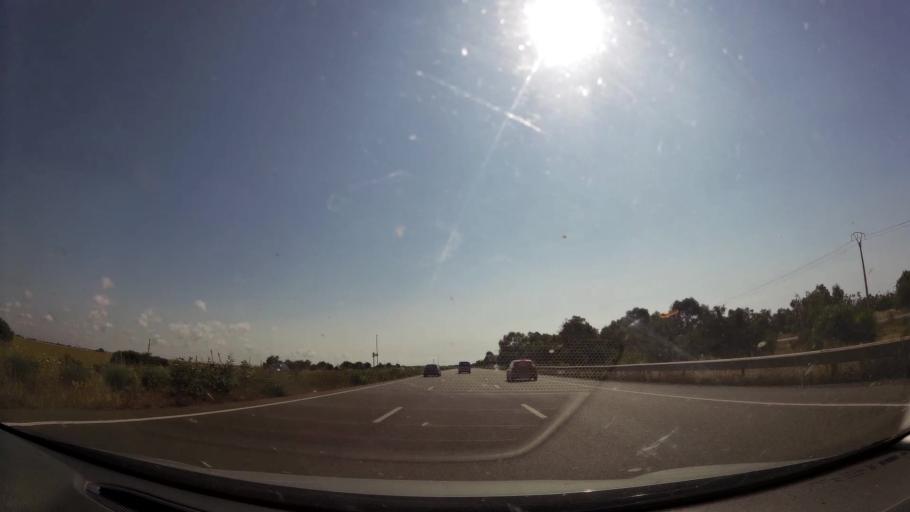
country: MA
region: Chaouia-Ouardigha
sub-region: Benslimane
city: Bouznika
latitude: 33.7880
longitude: -7.2101
